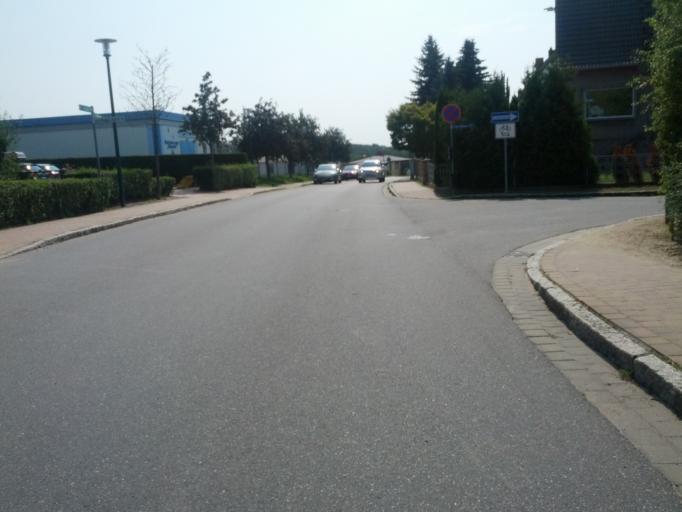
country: DE
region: Mecklenburg-Vorpommern
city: Bastorf
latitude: 54.1022
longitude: 11.6225
